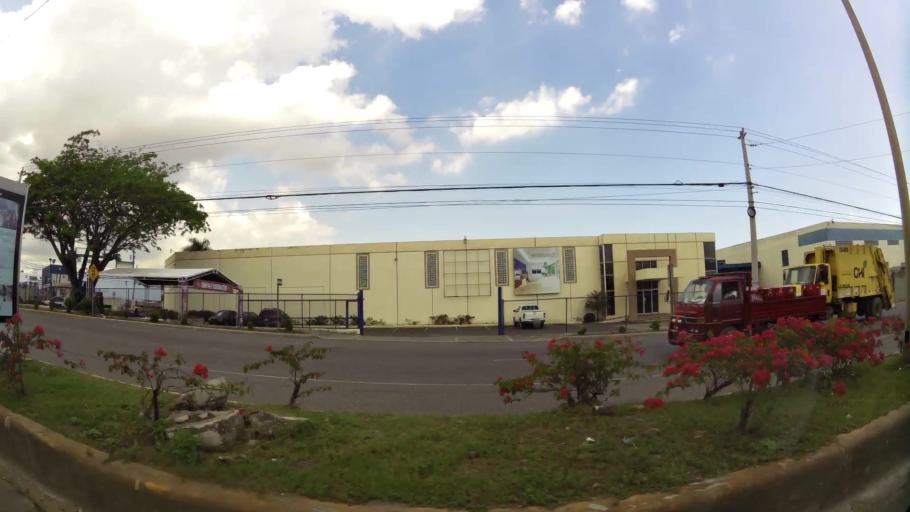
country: DO
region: Santo Domingo
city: Santo Domingo Oeste
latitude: 18.4975
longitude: -69.9993
